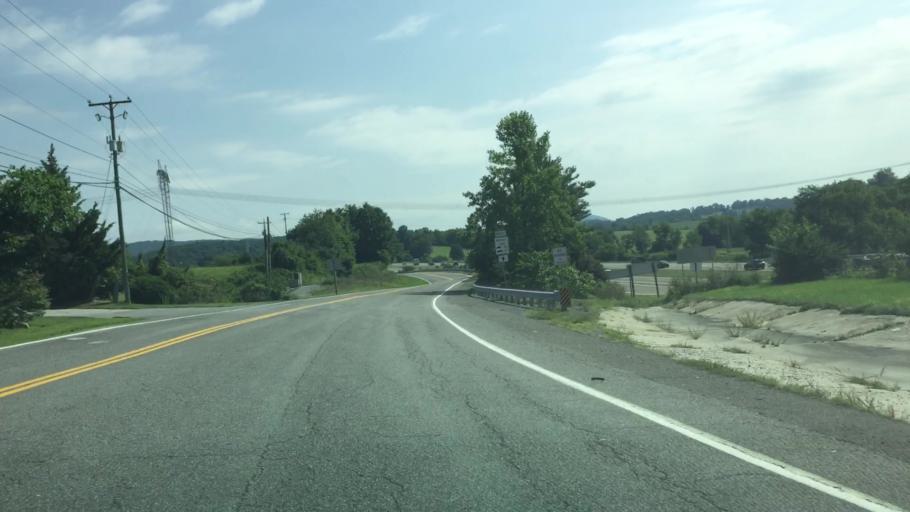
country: US
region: Virginia
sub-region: Pulaski County
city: Pulaski
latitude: 36.9661
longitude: -80.8526
